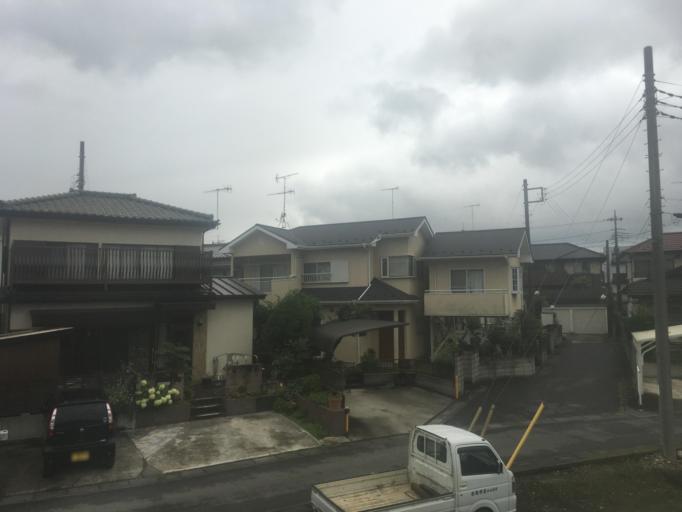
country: JP
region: Saitama
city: Yorii
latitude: 36.1341
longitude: 139.2568
